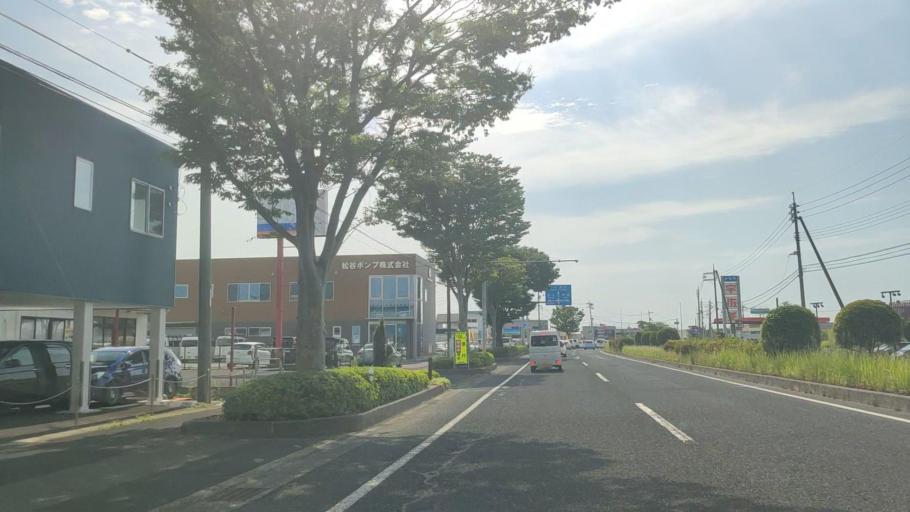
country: JP
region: Tottori
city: Tottori
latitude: 35.5197
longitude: 134.1946
